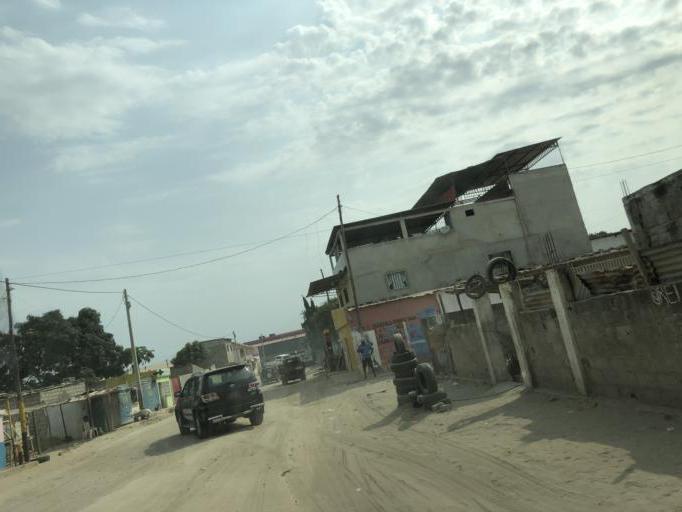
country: AO
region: Luanda
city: Luanda
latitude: -8.9009
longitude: 13.3486
